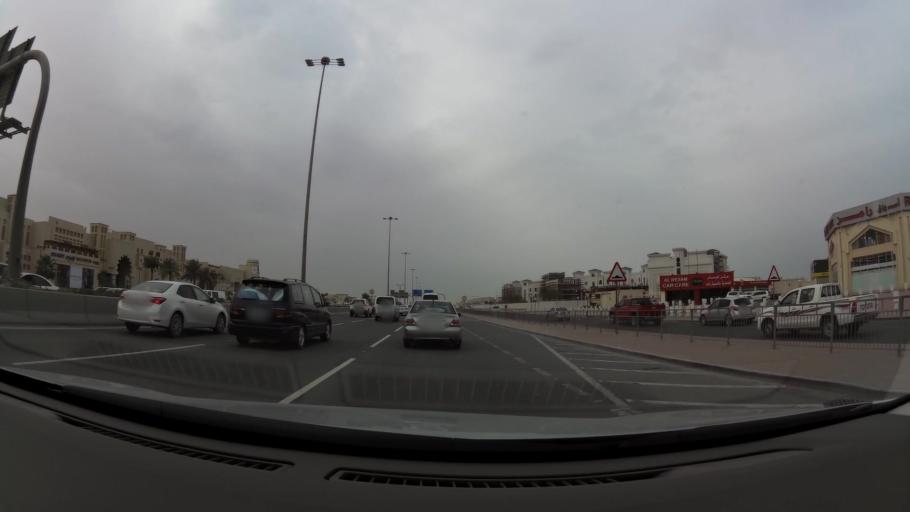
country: QA
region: Baladiyat ar Rayyan
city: Ar Rayyan
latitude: 25.3356
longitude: 51.4626
